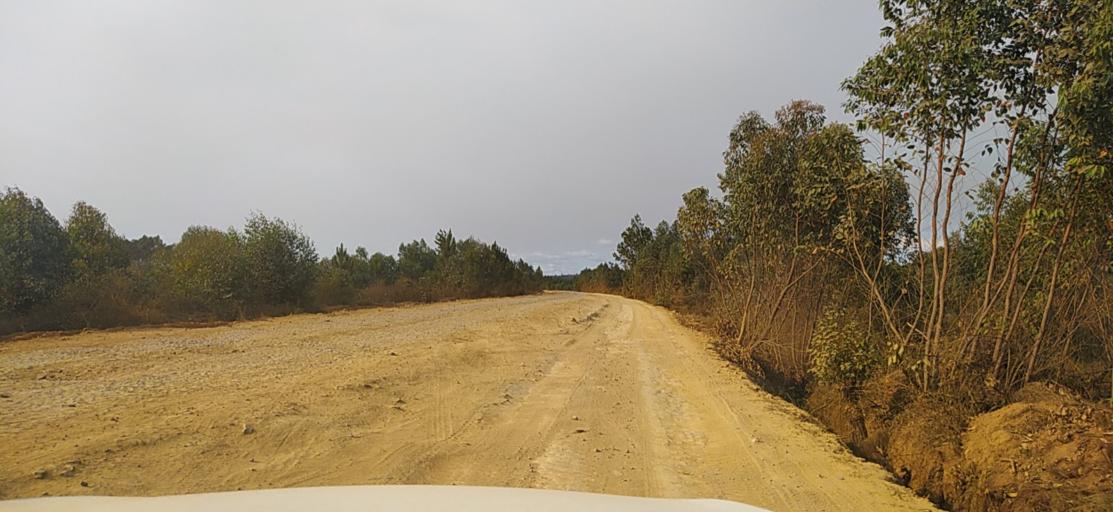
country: MG
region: Alaotra Mangoro
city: Moramanga
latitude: -18.6477
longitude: 48.2747
